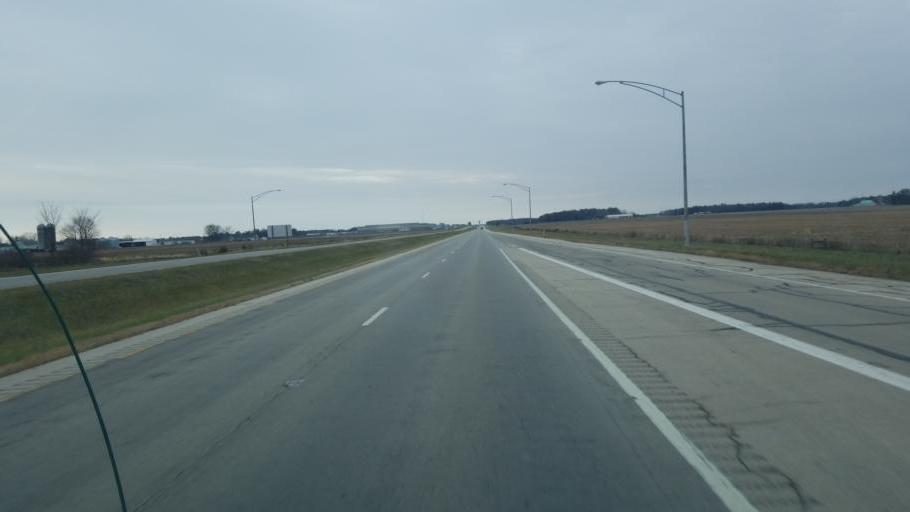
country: US
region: Ohio
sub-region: Auglaize County
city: Saint Marys
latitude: 40.5574
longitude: -84.4483
